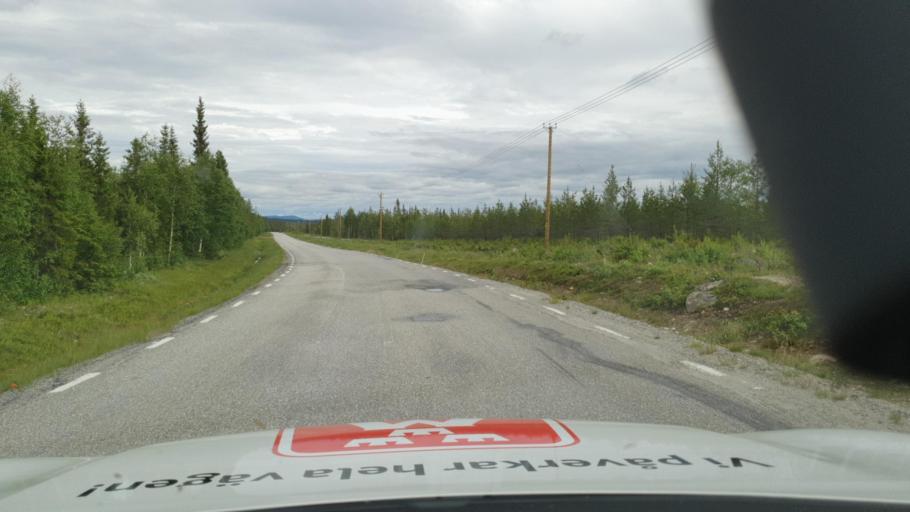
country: SE
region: Vaesterbotten
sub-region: Lycksele Kommun
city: Soderfors
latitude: 64.3815
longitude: 18.0220
